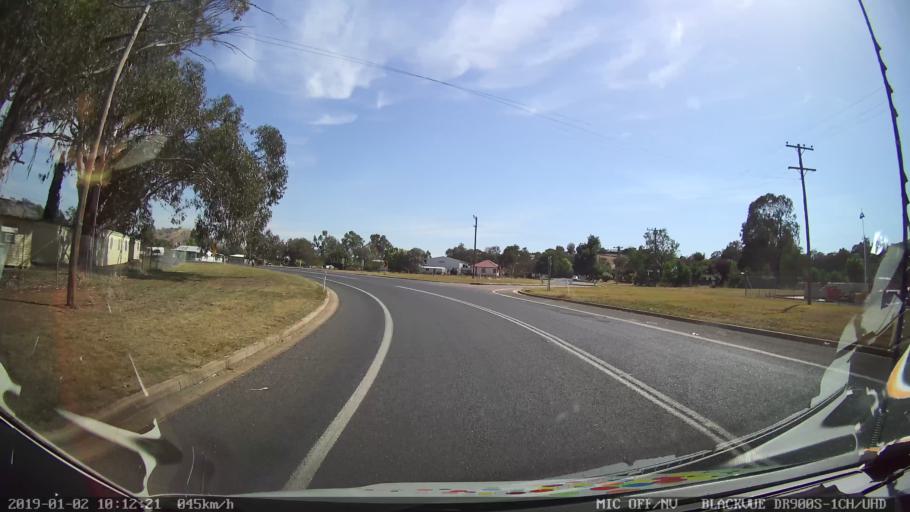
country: AU
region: New South Wales
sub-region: Gundagai
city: Gundagai
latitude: -35.0853
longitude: 148.0951
